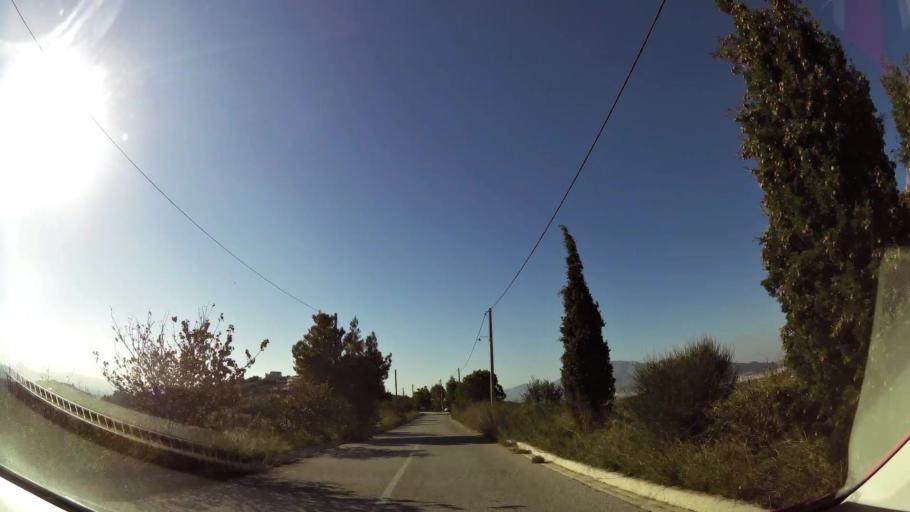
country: GR
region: Attica
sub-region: Nomarchia Anatolikis Attikis
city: Anthousa
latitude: 38.0348
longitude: 23.8922
